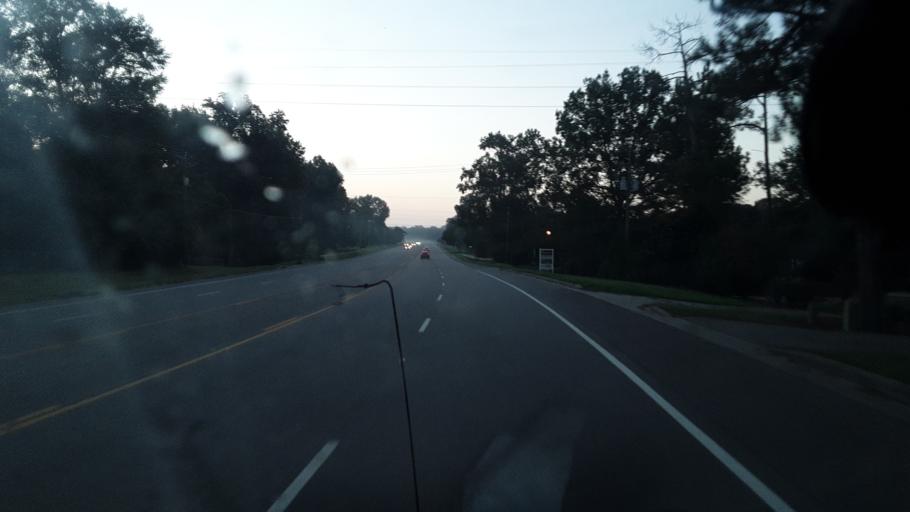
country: US
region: South Carolina
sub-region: Sumter County
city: Lakewood
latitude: 33.8706
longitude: -80.3276
